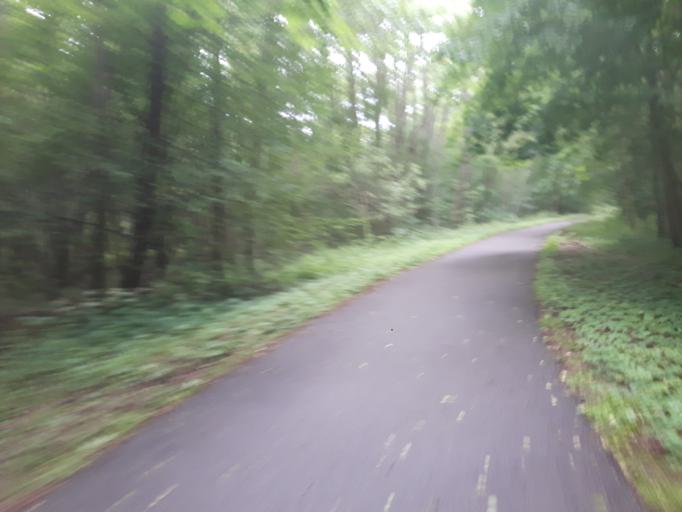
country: LT
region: Klaipedos apskritis
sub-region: Klaipeda
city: Palanga
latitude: 55.8570
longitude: 21.0630
